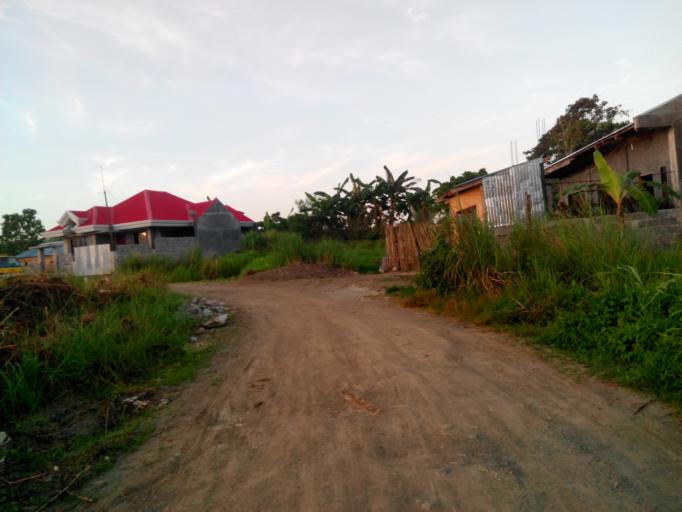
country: PH
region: Western Visayas
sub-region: Province of Iloilo
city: Passi
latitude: 11.1224
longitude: 122.6474
